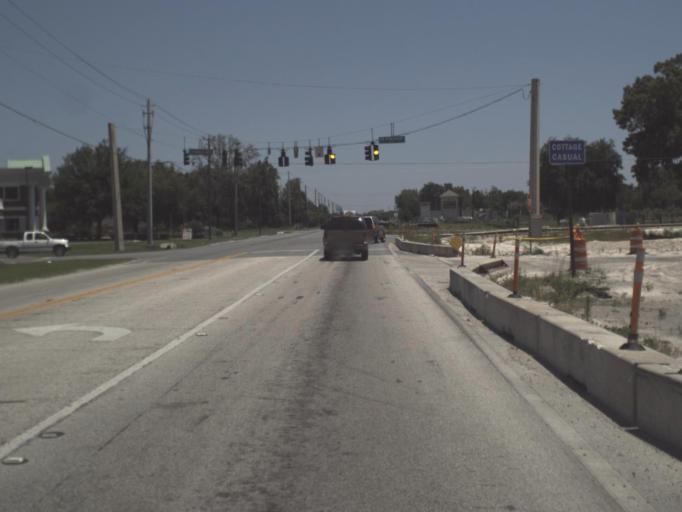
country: US
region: Florida
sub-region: Columbia County
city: Lake City
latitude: 30.1849
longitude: -82.7104
